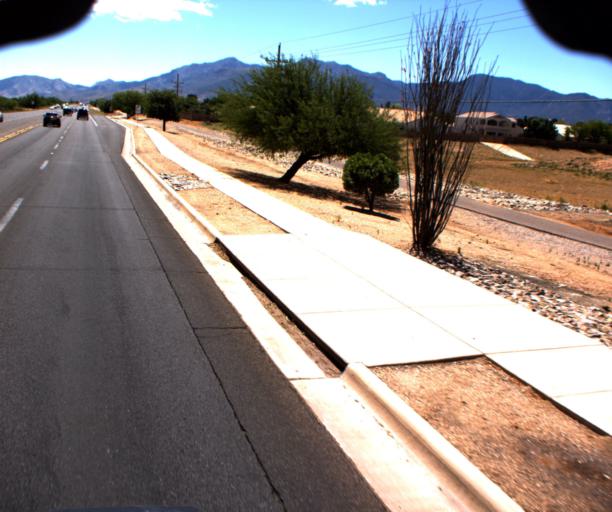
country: US
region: Arizona
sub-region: Cochise County
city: Sierra Vista
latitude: 31.5277
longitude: -110.2574
